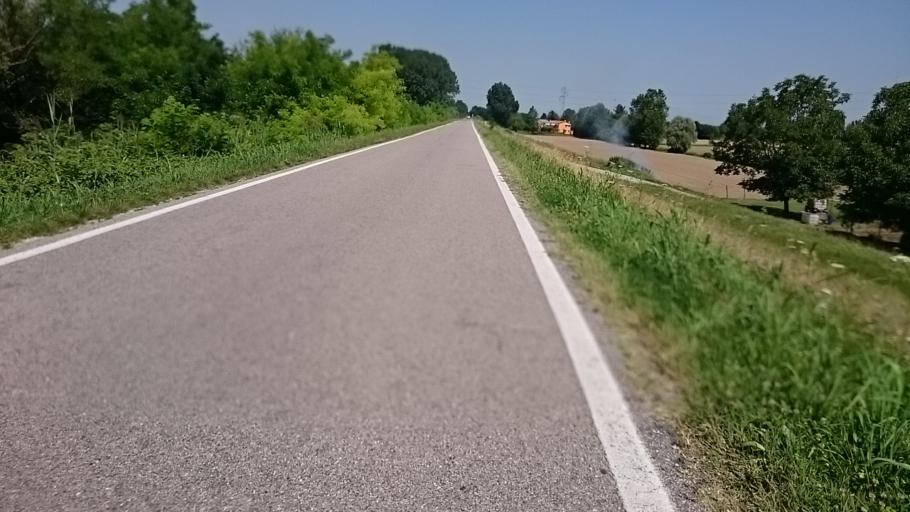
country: IT
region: Veneto
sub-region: Provincia di Venezia
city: Galta
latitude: 45.3792
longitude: 12.0232
